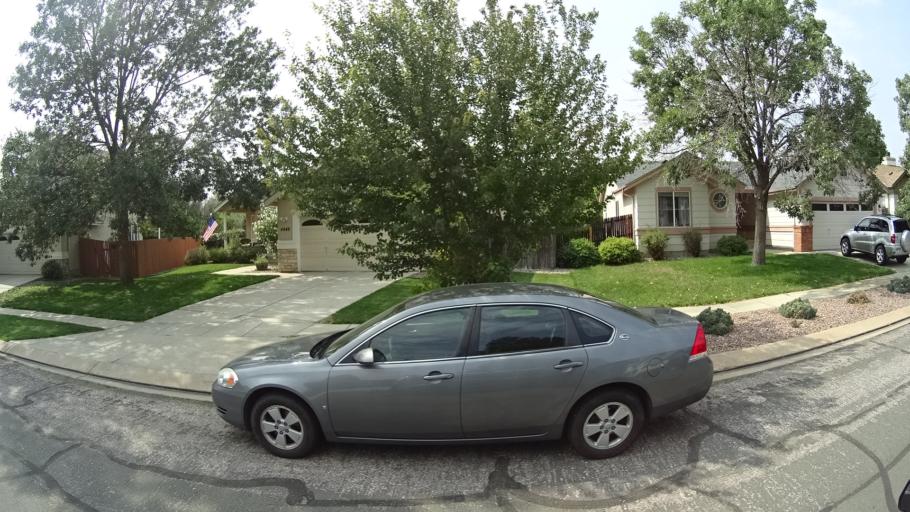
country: US
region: Colorado
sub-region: El Paso County
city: Cimarron Hills
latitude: 38.8194
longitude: -104.7424
